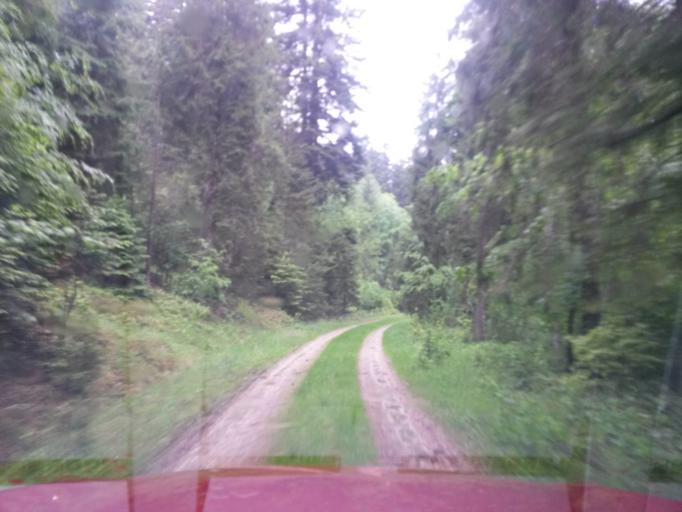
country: SK
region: Kosicky
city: Medzev
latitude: 48.7833
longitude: 20.7868
